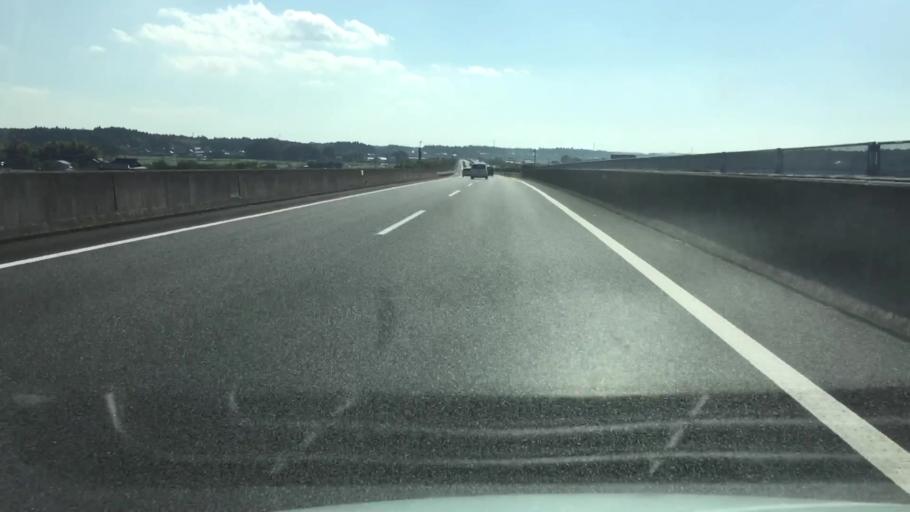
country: JP
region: Ibaraki
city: Tomobe
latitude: 36.3271
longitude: 140.2955
